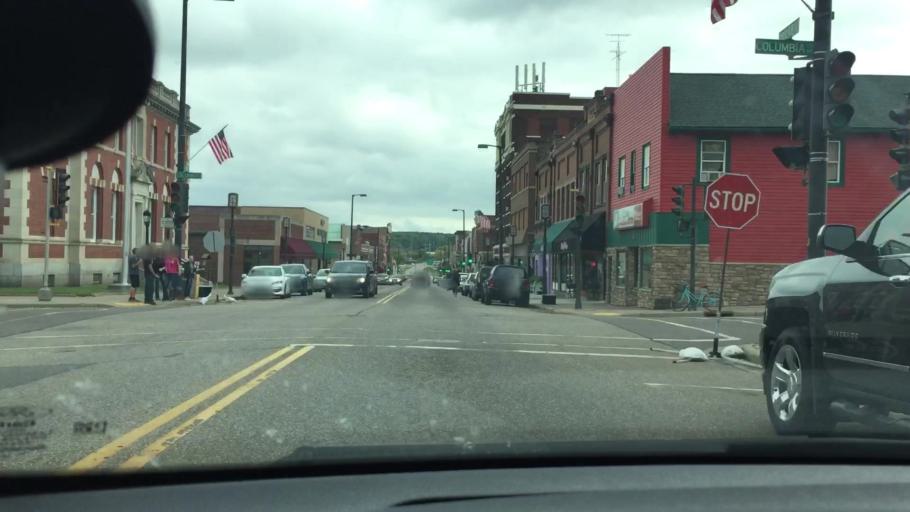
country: US
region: Wisconsin
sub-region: Chippewa County
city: Chippewa Falls
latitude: 44.9379
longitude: -91.3943
